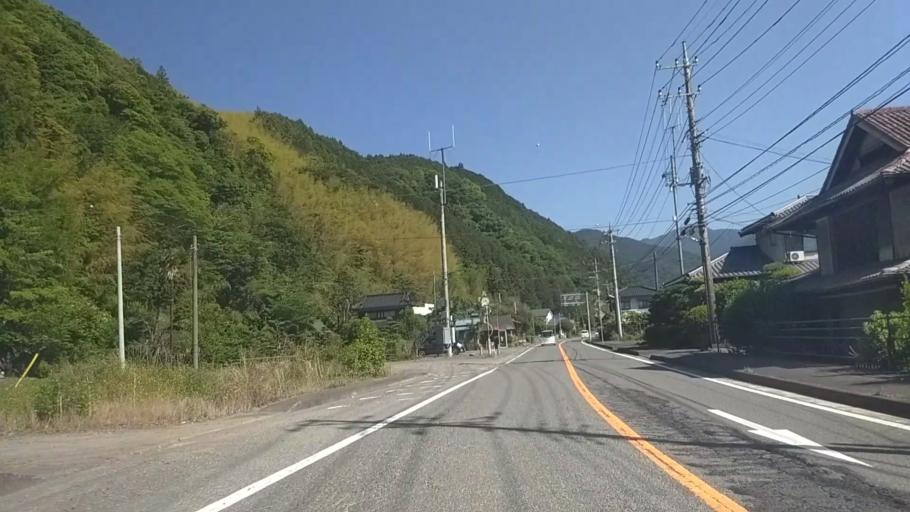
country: JP
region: Shizuoka
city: Fujinomiya
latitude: 35.2260
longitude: 138.5092
